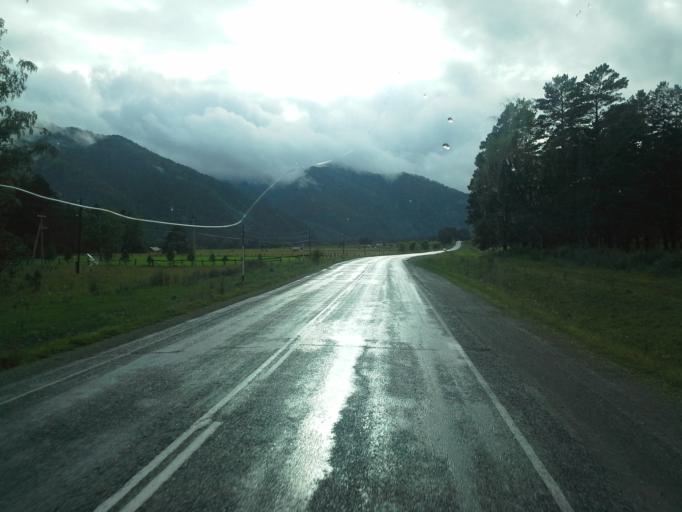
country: RU
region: Altay
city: Elekmonar
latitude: 51.5696
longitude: 85.8911
